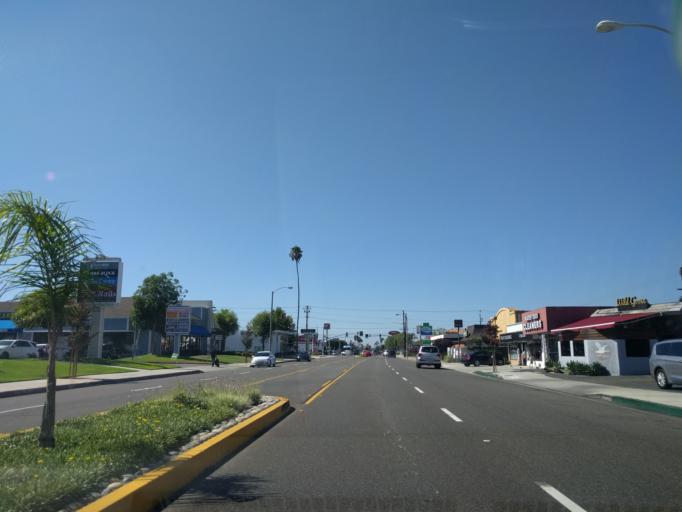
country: US
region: California
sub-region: Orange County
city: Costa Mesa
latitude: 33.6298
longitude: -117.9105
